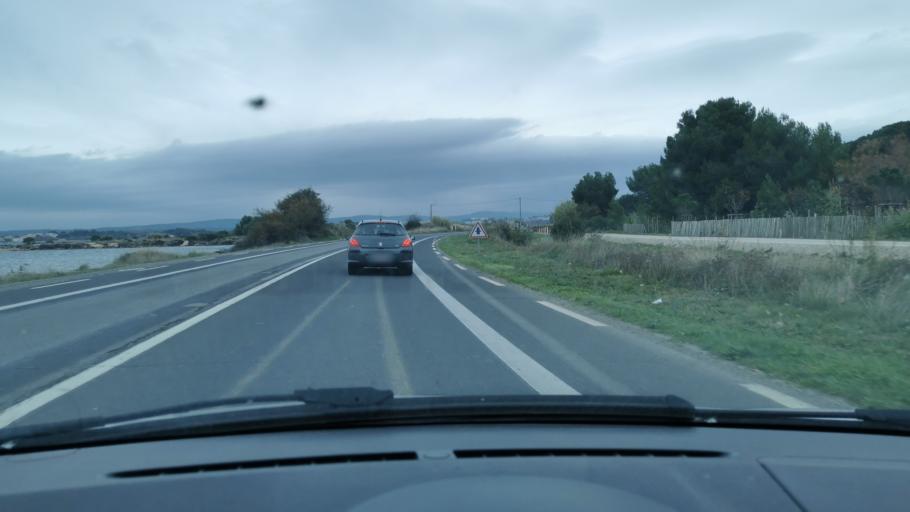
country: FR
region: Languedoc-Roussillon
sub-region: Departement de l'Herault
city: Balaruc-les-Bains
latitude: 43.4319
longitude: 3.7034
